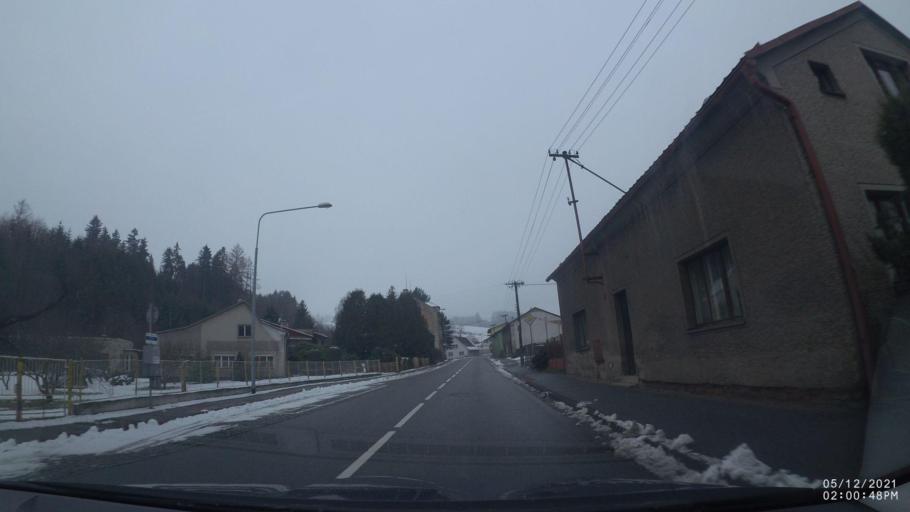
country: CZ
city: Hronov
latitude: 50.4814
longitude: 16.1617
